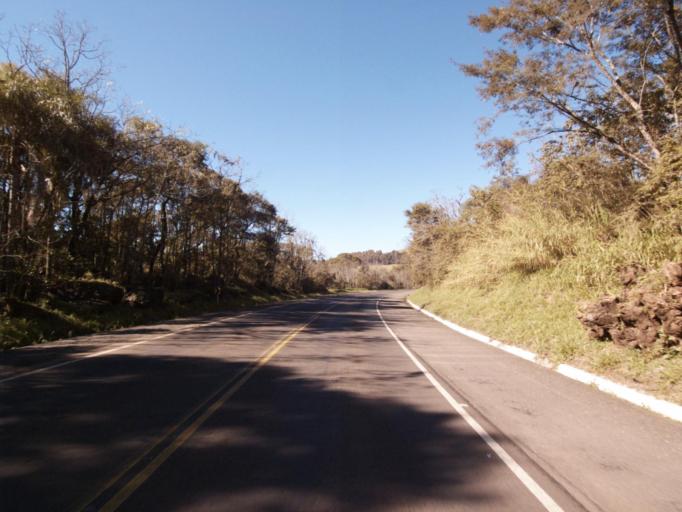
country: BR
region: Rio Grande do Sul
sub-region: Frederico Westphalen
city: Frederico Westphalen
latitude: -26.7983
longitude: -53.3213
